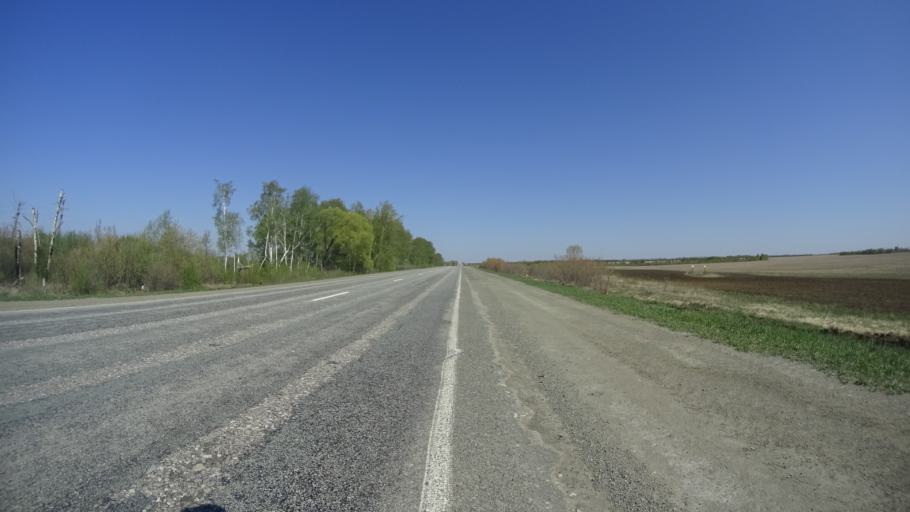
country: RU
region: Chelyabinsk
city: Troitsk
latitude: 54.1967
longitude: 61.4327
